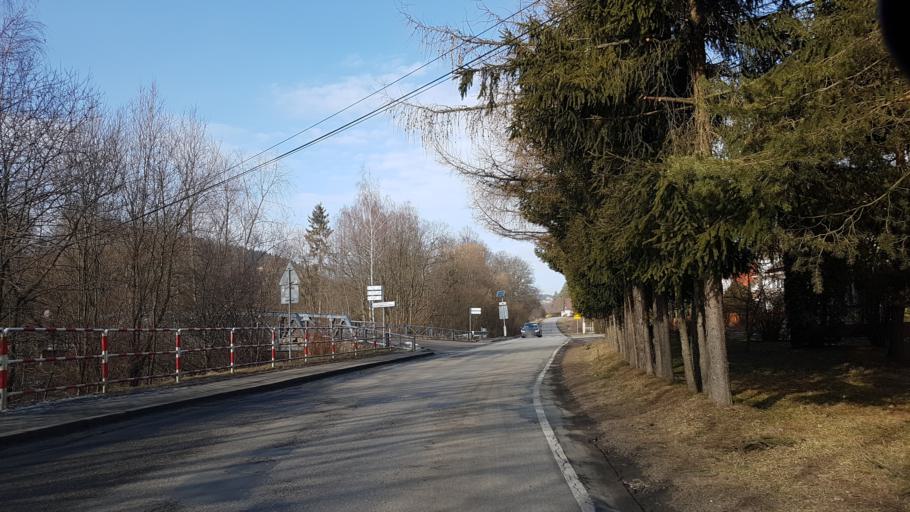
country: PL
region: Lesser Poland Voivodeship
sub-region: Powiat limanowski
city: Lukowica
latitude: 49.6617
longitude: 20.4859
